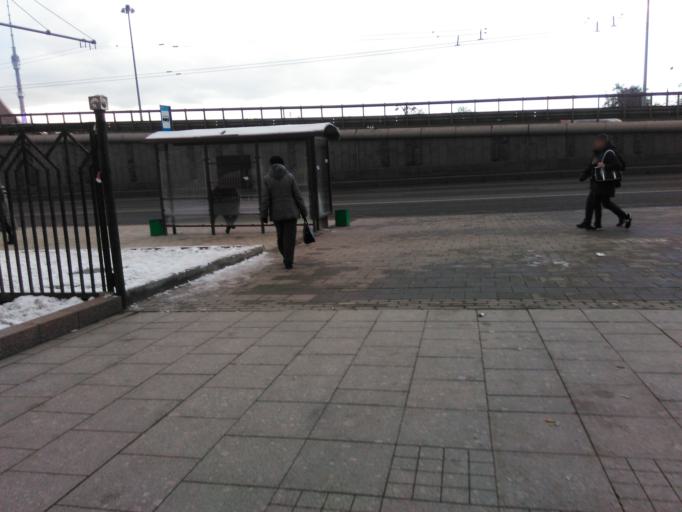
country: RU
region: Moscow
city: Rostokino
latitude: 55.8231
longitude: 37.6445
